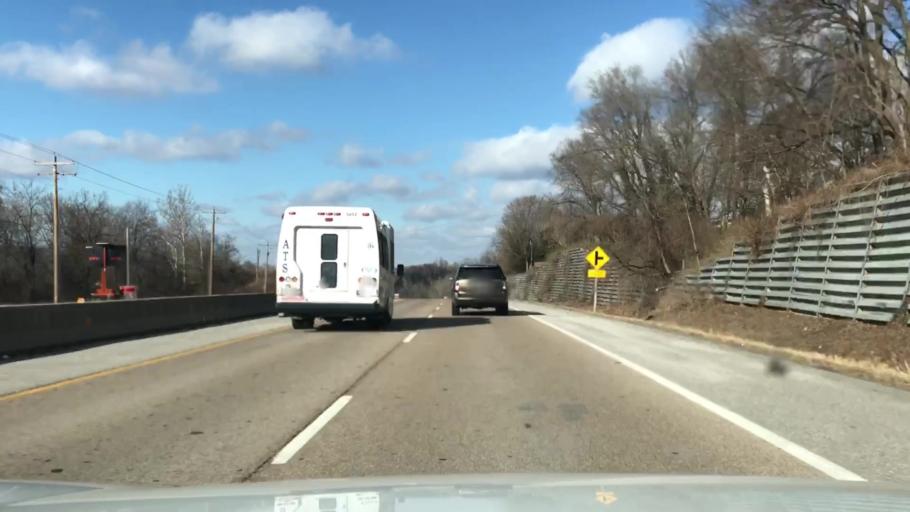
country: US
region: Illinois
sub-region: Saint Clair County
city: Fairview Heights
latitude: 38.5781
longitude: -90.0371
